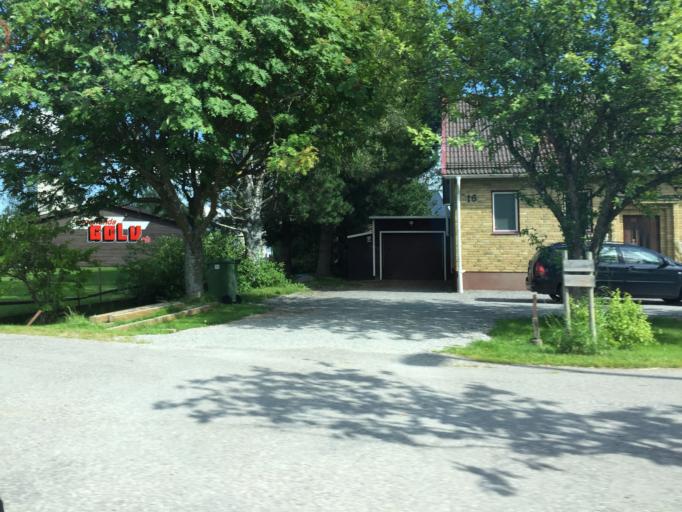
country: SE
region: Gaevleborg
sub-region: Bollnas Kommun
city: Arbra
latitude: 61.5155
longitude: 16.3626
